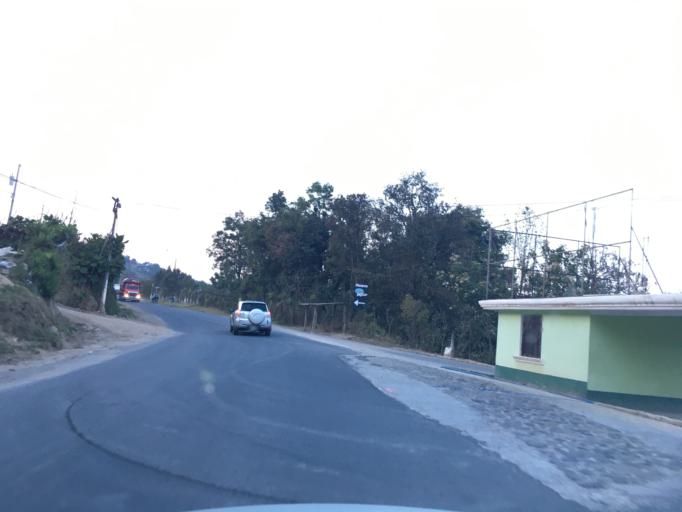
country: GT
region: Chimaltenango
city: Tecpan Guatemala
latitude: 14.7463
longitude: -91.0006
